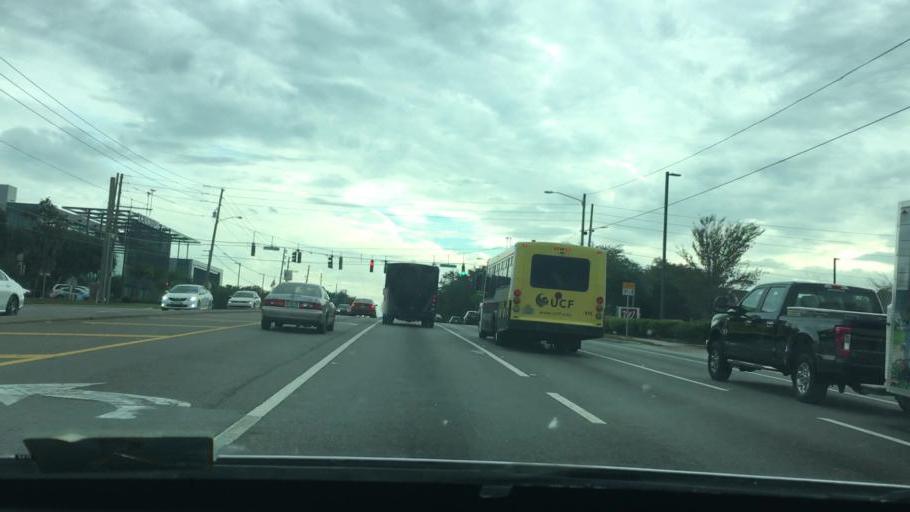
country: US
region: Florida
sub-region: Orange County
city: Alafaya
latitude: 28.5840
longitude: -81.2078
